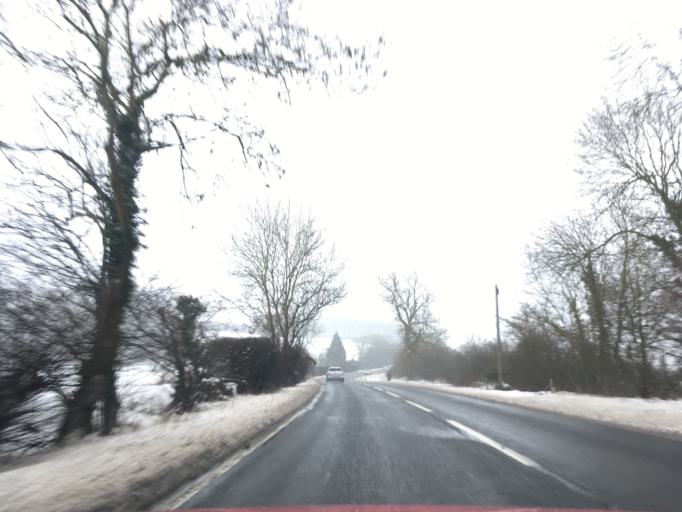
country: GB
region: England
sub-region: Warwickshire
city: Stratford-upon-Avon
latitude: 52.2008
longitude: -1.7757
